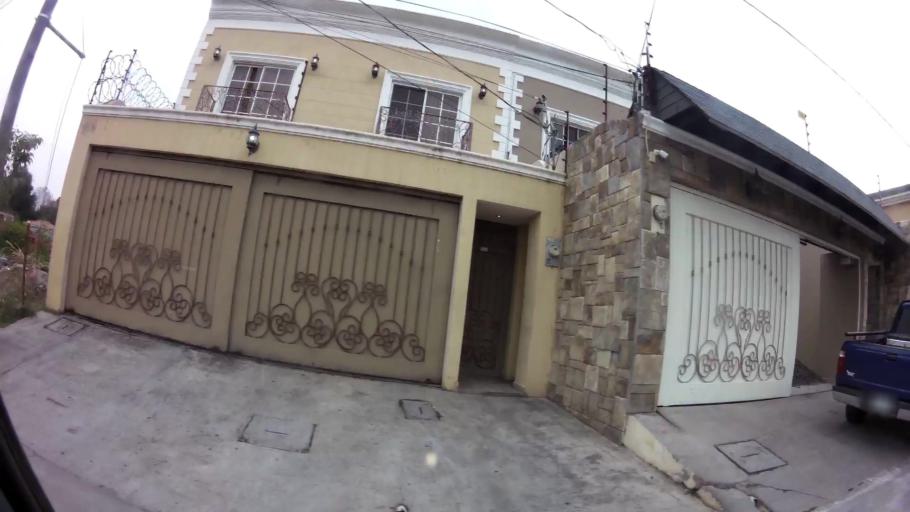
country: HN
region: Francisco Morazan
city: Tegucigalpa
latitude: 14.0793
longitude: -87.1786
